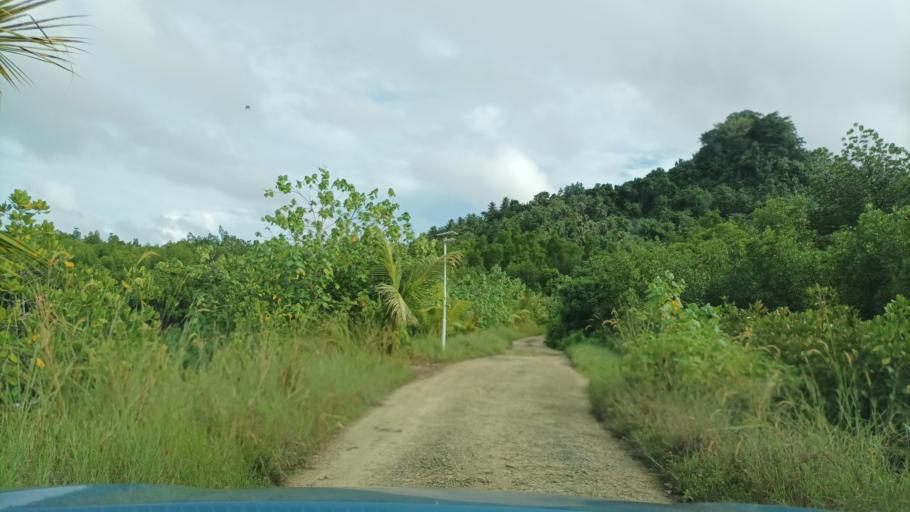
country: FM
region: Pohnpei
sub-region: Kolonia Municipality
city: Kolonia
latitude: 6.9326
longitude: 158.2870
